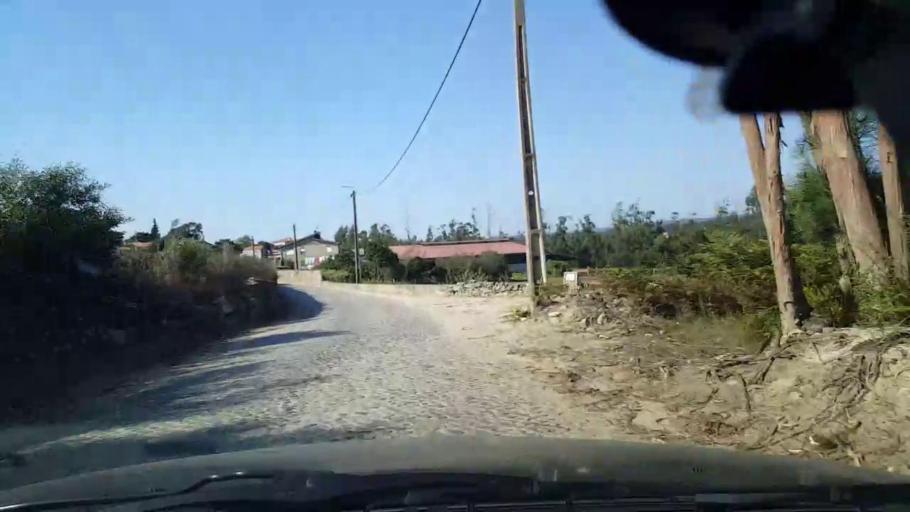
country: PT
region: Porto
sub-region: Vila do Conde
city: Arvore
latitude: 41.3606
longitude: -8.6956
